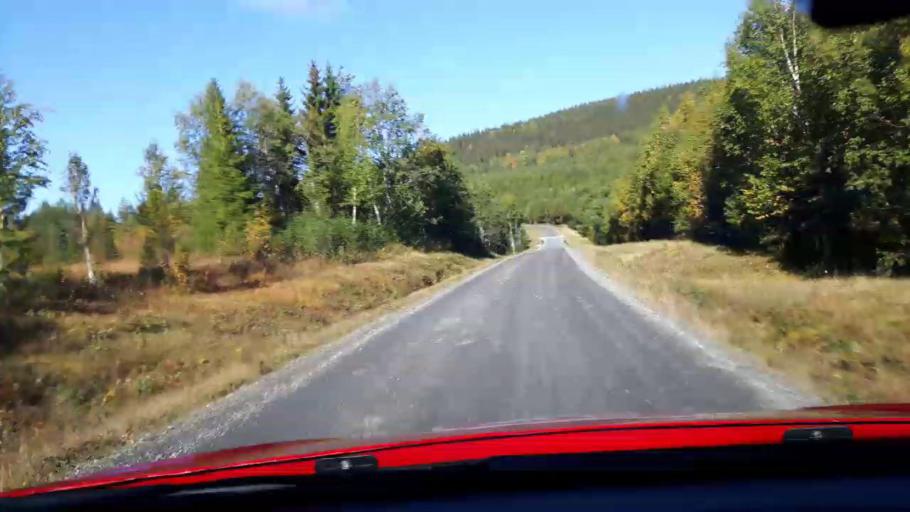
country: NO
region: Nord-Trondelag
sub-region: Lierne
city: Sandvika
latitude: 64.5890
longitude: 13.8597
